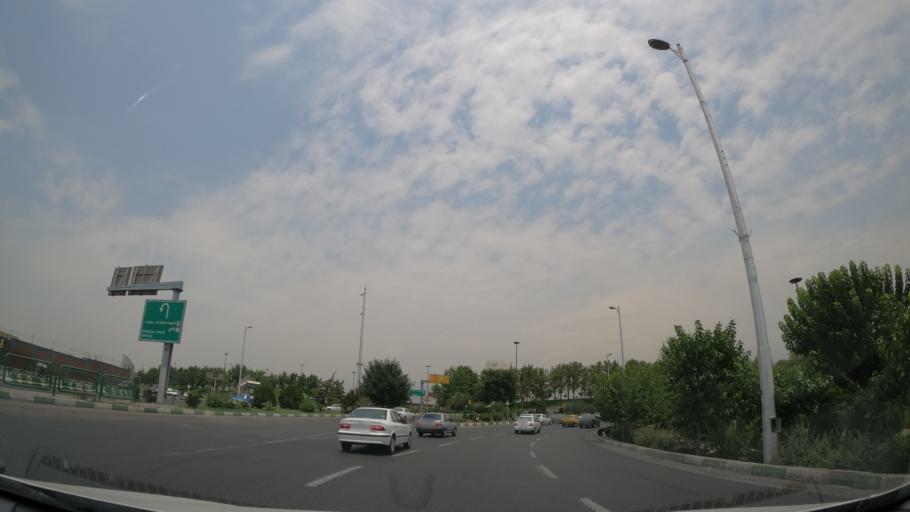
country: IR
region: Tehran
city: Tehran
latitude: 35.6968
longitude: 51.3390
